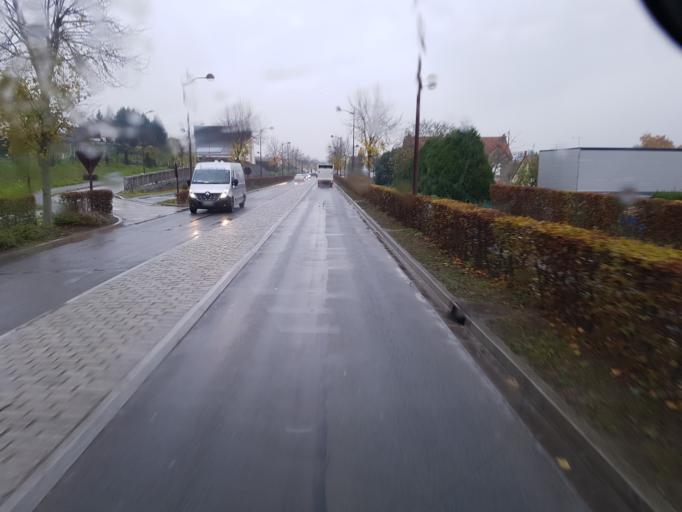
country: FR
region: Picardie
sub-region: Departement de l'Aisne
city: Saint-Quentin
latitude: 49.8511
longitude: 3.2707
